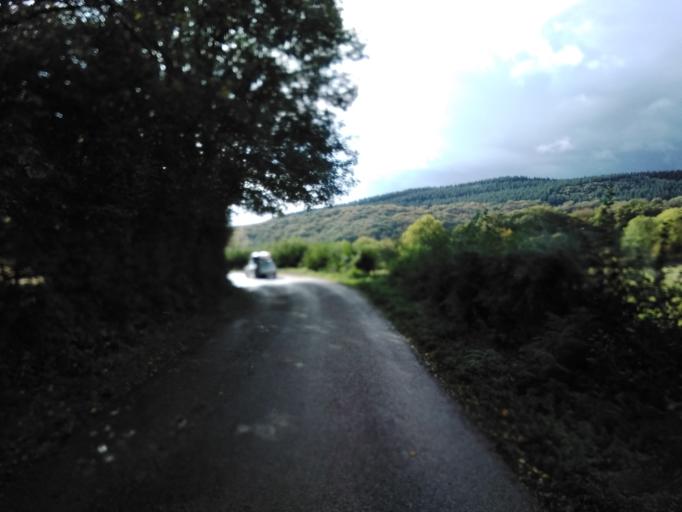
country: FR
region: Bourgogne
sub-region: Departement de la Nievre
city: Lormes
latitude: 47.2950
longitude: 3.8598
